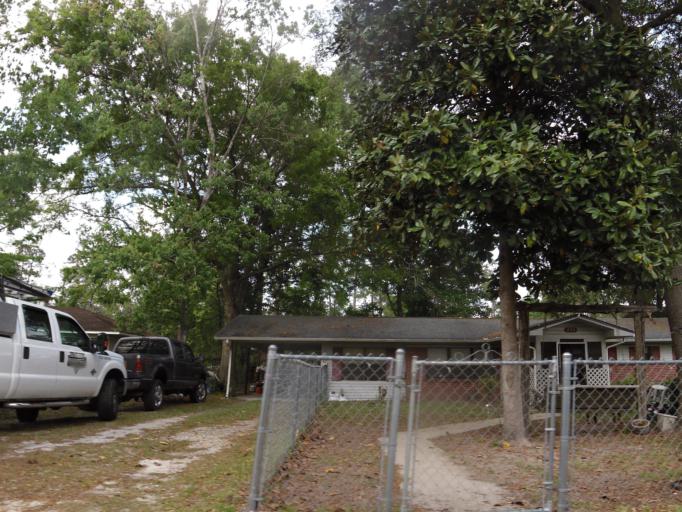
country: US
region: Georgia
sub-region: Charlton County
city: Folkston
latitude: 30.8334
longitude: -81.9863
